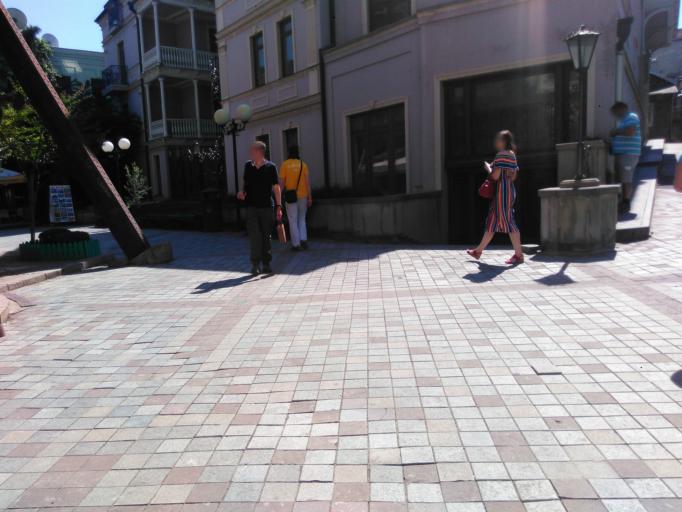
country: GE
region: T'bilisi
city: Tbilisi
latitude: 41.6959
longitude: 44.8065
